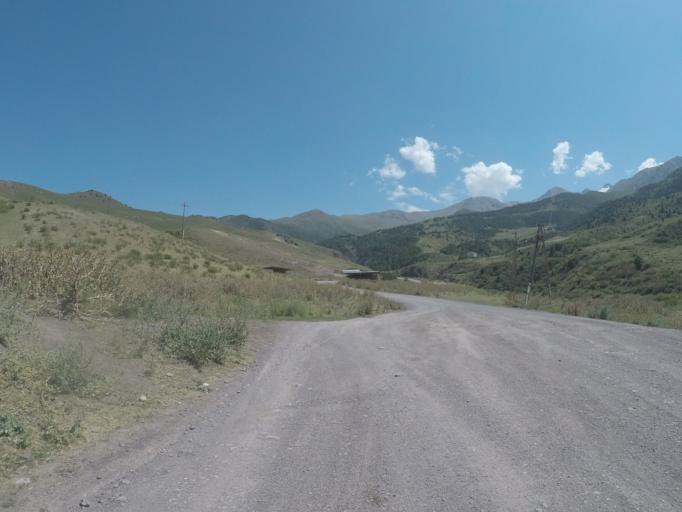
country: KG
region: Chuy
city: Bishkek
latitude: 42.6492
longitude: 74.5110
